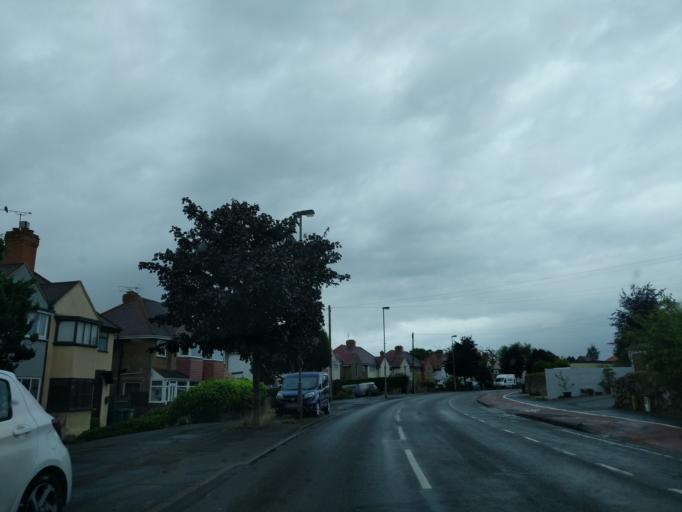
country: GB
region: England
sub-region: Staffordshire
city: Stafford
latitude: 52.8046
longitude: -2.0888
